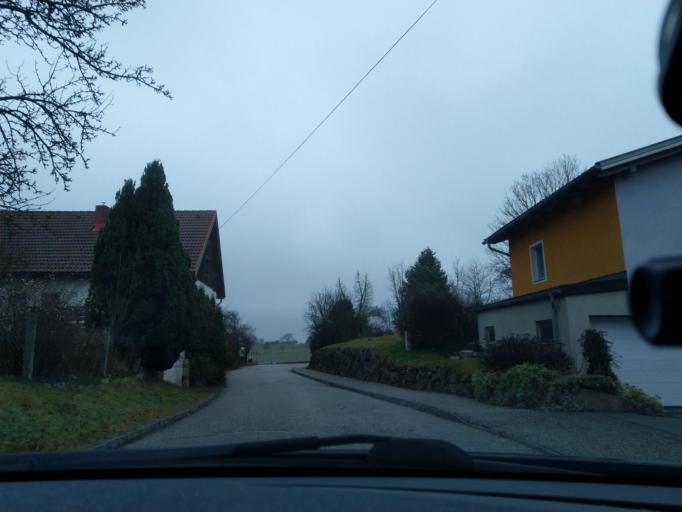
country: AT
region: Upper Austria
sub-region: Politischer Bezirk Urfahr-Umgebung
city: Engerwitzdorf
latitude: 48.3733
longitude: 14.5219
